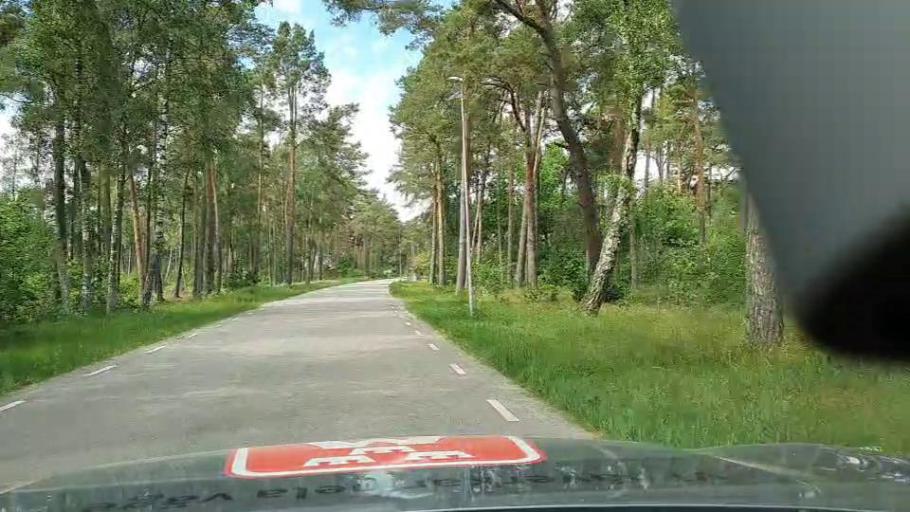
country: SE
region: Blekinge
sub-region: Karlshamns Kommun
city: Morrum
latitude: 56.0957
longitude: 14.6912
